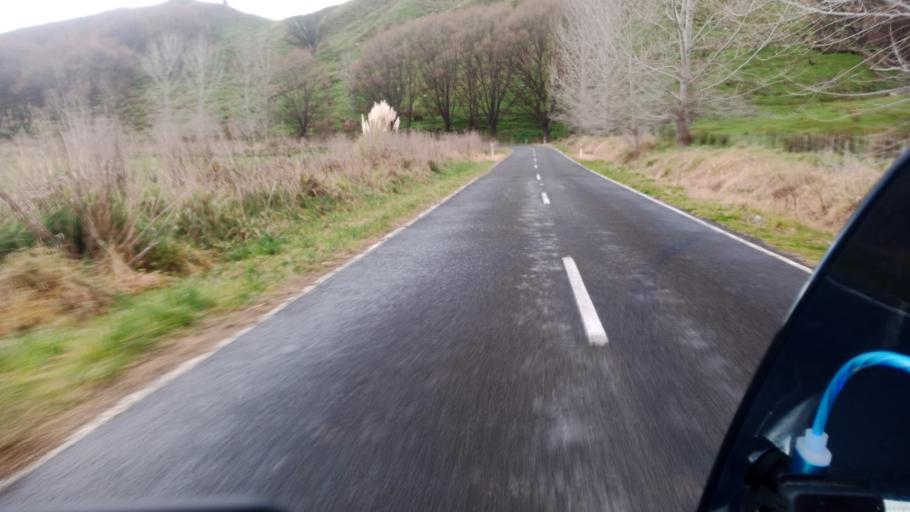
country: NZ
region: Gisborne
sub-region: Gisborne District
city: Gisborne
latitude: -38.3272
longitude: 178.3118
